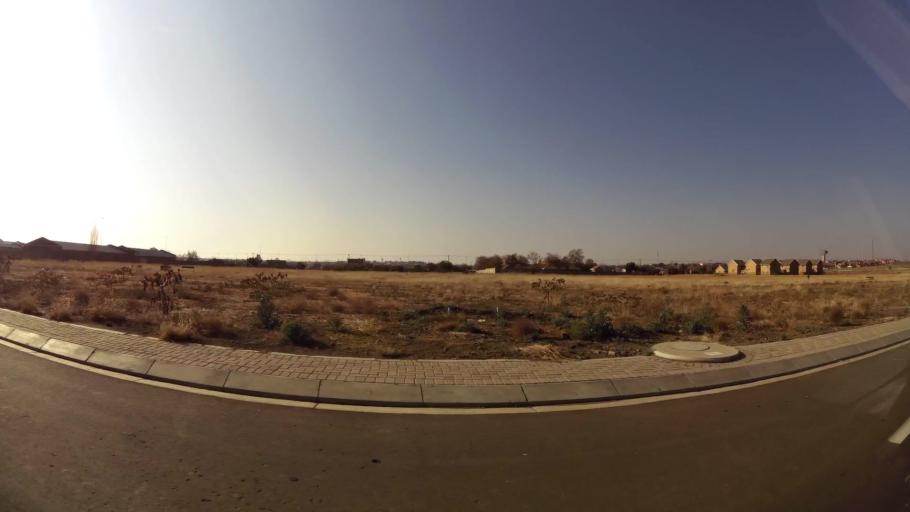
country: ZA
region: Orange Free State
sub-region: Mangaung Metropolitan Municipality
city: Bloemfontein
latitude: -29.1895
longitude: 26.2193
